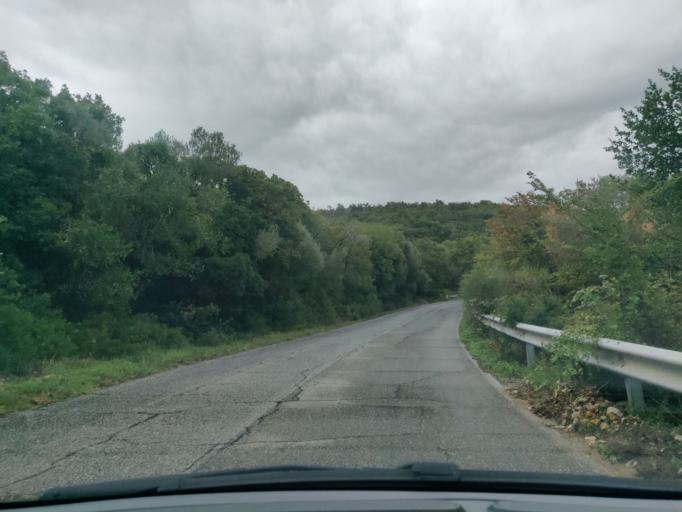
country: IT
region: Latium
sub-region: Citta metropolitana di Roma Capitale
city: Allumiere
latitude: 42.1300
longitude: 11.8503
